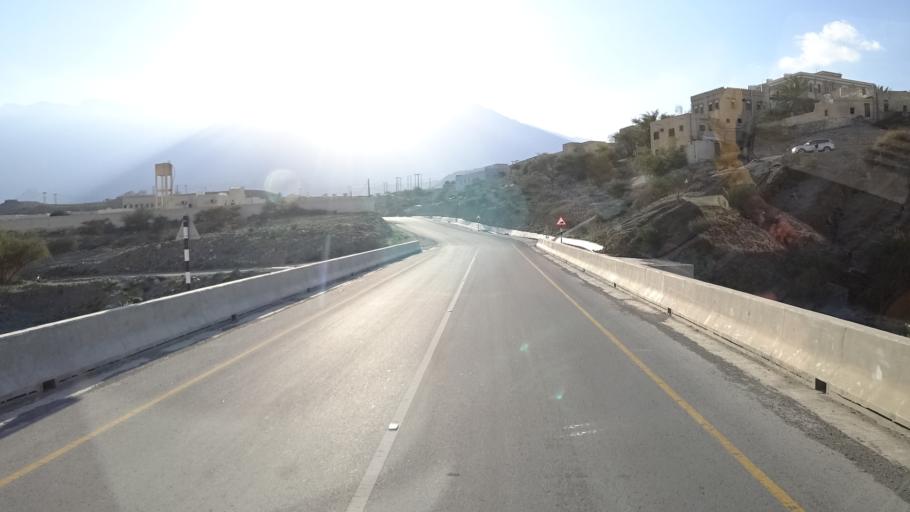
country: OM
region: Al Batinah
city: Rustaq
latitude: 23.2859
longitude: 57.3329
